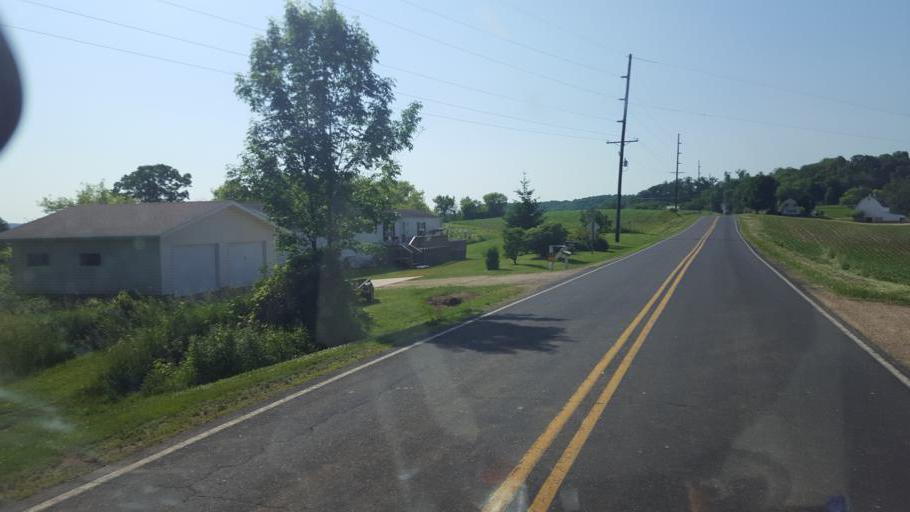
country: US
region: Wisconsin
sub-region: Vernon County
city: Hillsboro
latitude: 43.6644
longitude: -90.3472
